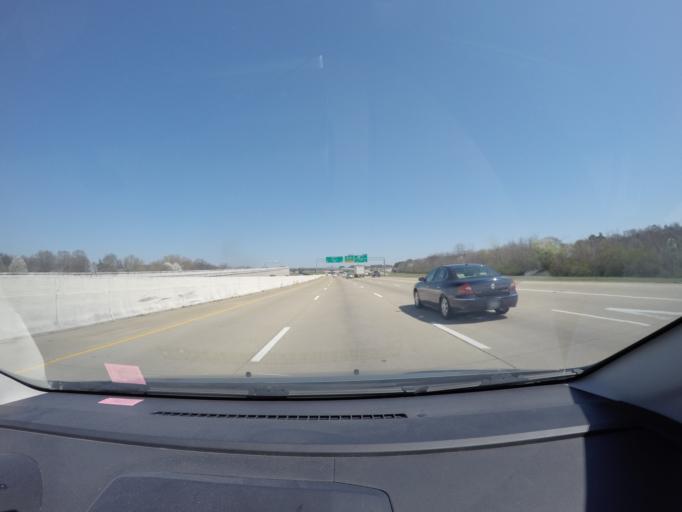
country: US
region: Tennessee
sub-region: Hamilton County
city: East Brainerd
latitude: 35.0221
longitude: -85.1751
